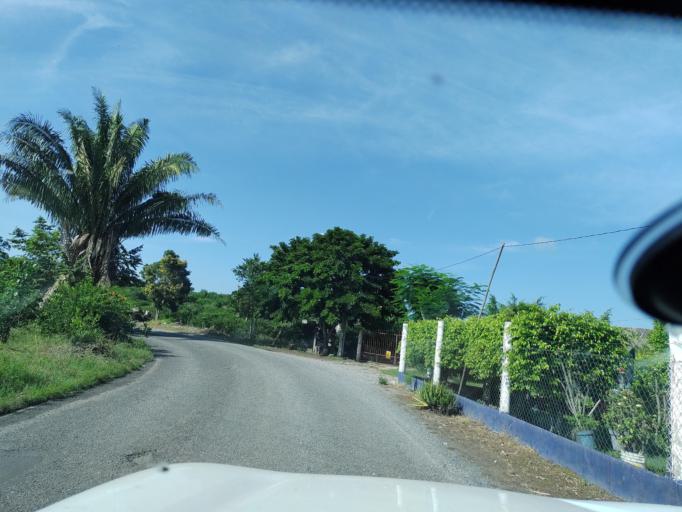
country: MX
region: Veracruz
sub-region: Martinez de la Torre
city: El Progreso
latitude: 20.1123
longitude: -96.9899
